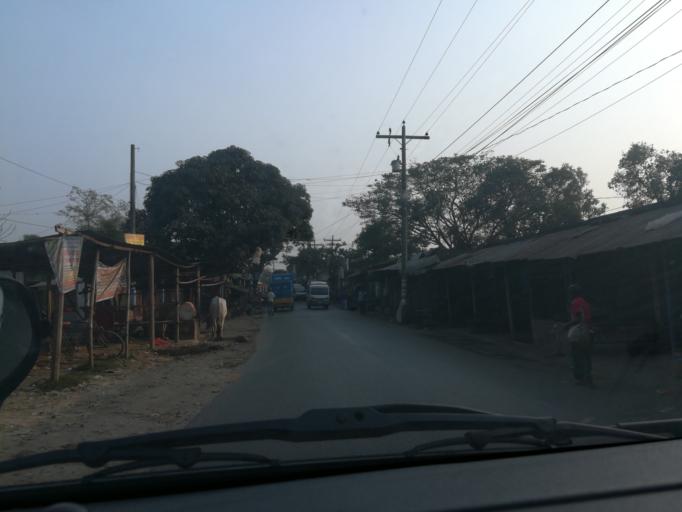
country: BD
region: Dhaka
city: Tungi
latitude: 23.8582
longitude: 90.3111
